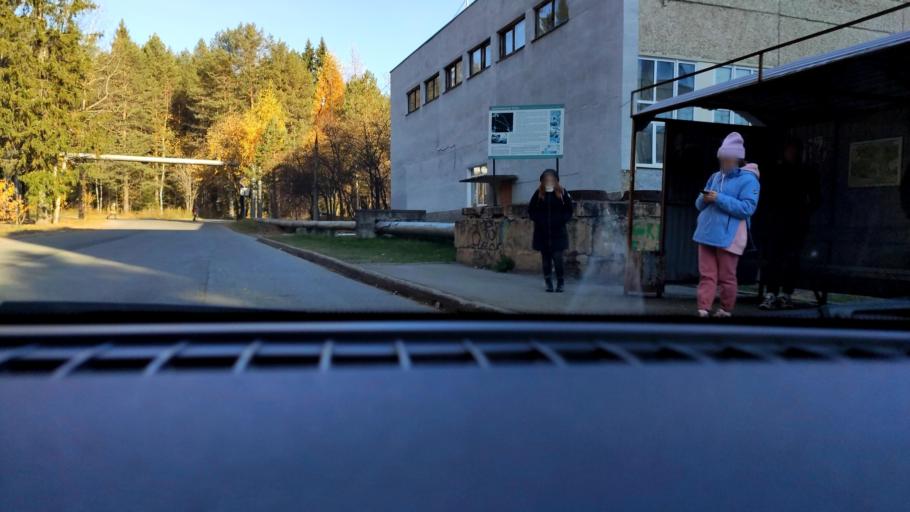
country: RU
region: Perm
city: Perm
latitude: 58.0541
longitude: 56.2306
